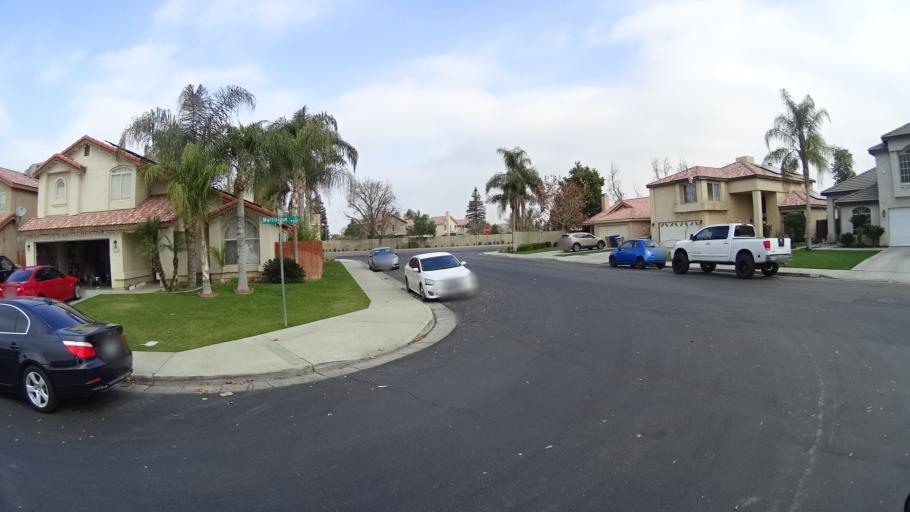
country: US
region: California
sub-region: Kern County
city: Greenfield
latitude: 35.3027
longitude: -119.0707
